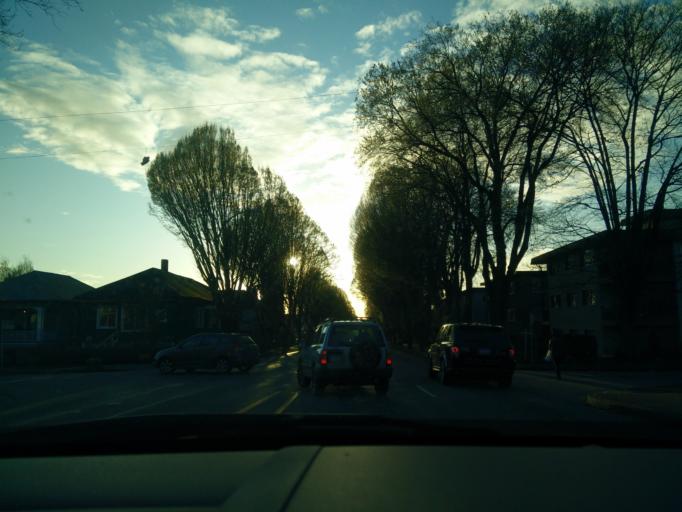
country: CA
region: British Columbia
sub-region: Fraser Valley Regional District
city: North Vancouver
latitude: 49.2697
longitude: -123.0711
